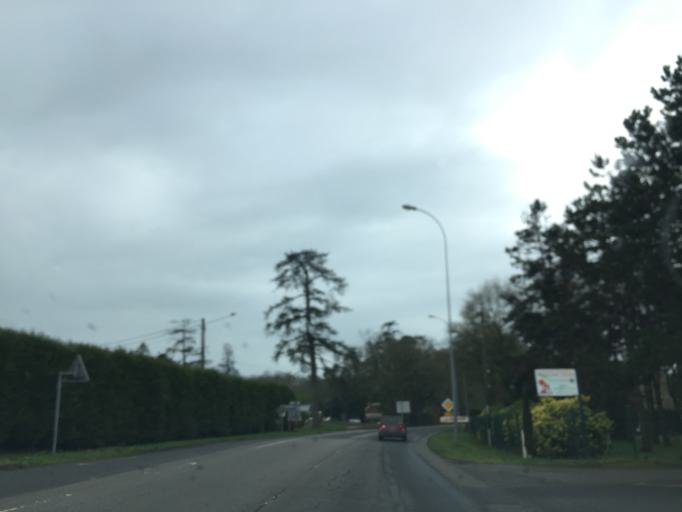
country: FR
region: Pays de la Loire
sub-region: Departement de la Loire-Atlantique
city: Chateaubriant
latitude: 47.6993
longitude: -1.3817
